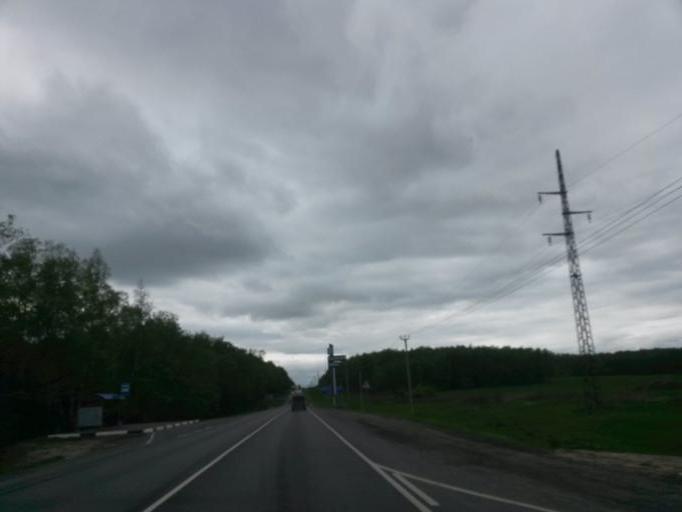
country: RU
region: Moskovskaya
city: Domodedovo
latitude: 55.3319
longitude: 37.7032
